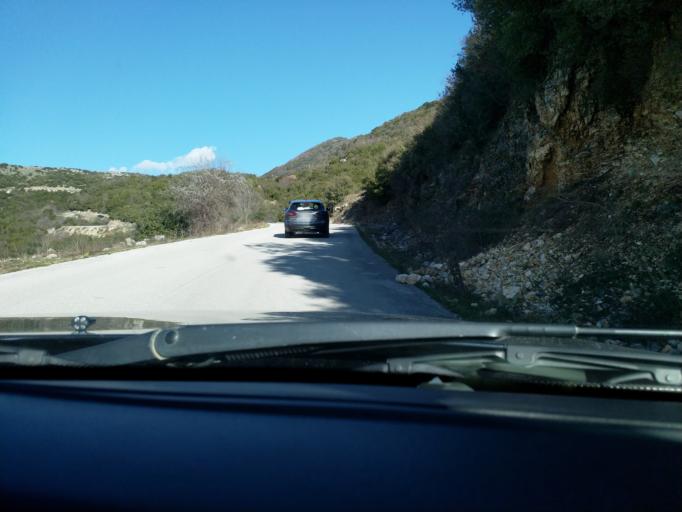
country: GR
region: Epirus
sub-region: Nomos Ioanninon
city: Kalpaki
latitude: 39.9018
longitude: 20.6716
